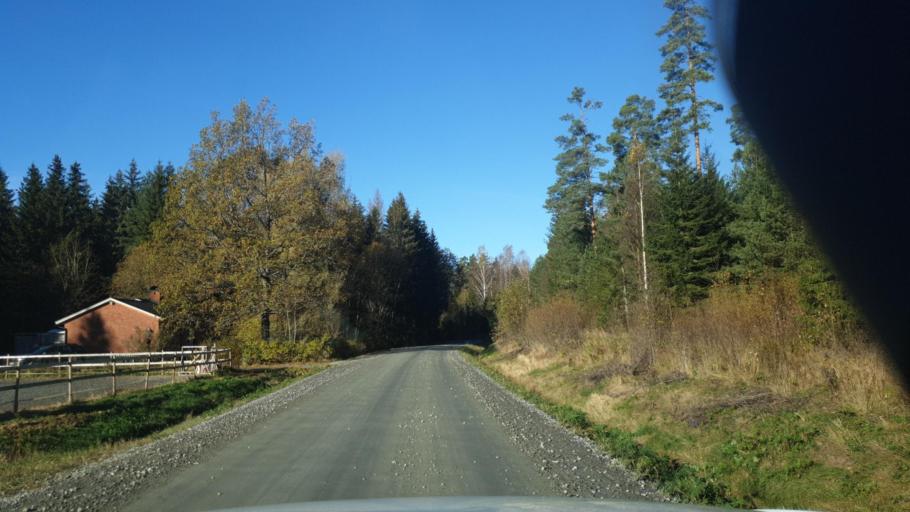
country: SE
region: Vaermland
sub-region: Karlstads Kommun
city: Edsvalla
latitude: 59.4505
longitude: 13.1502
